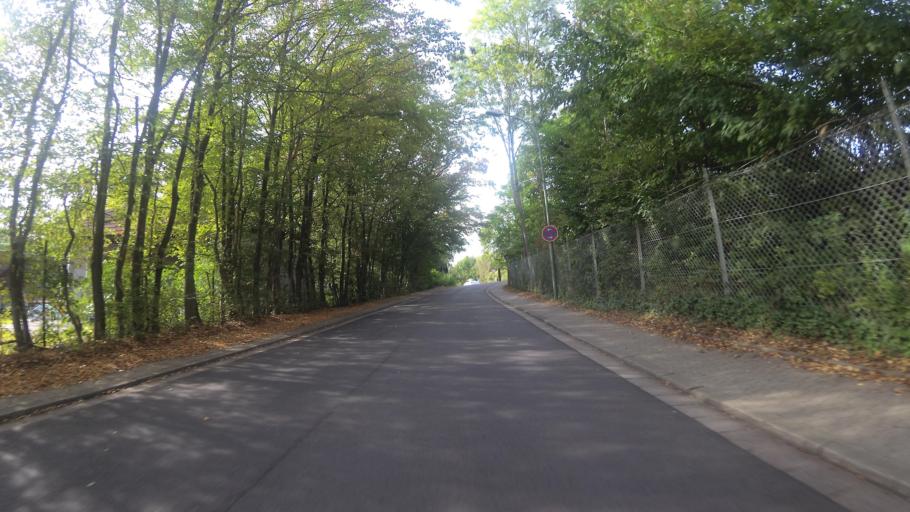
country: DE
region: Saarland
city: Sulzbach
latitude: 49.2887
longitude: 7.0790
